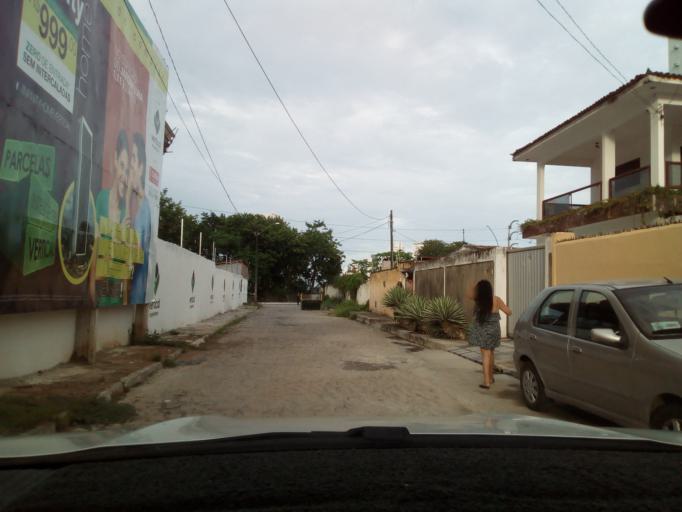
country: BR
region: Paraiba
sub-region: Joao Pessoa
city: Joao Pessoa
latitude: -7.1083
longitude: -34.8419
